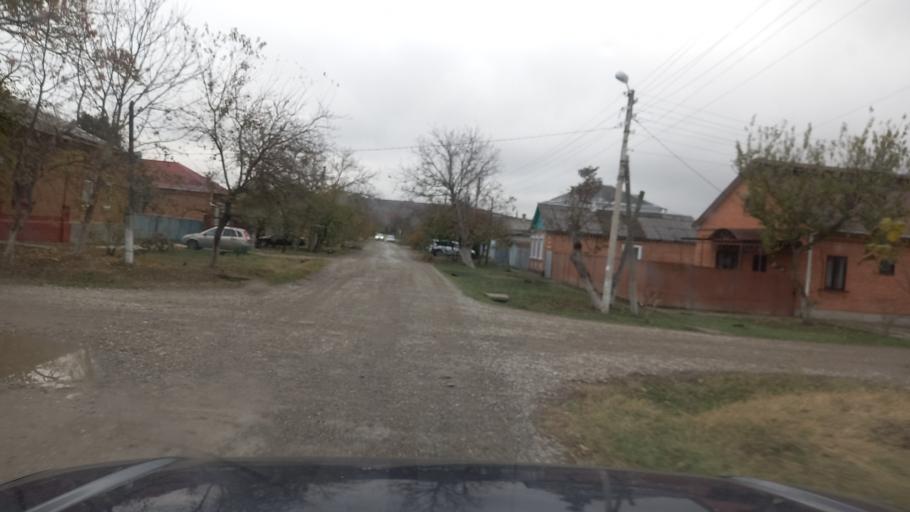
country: RU
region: Adygeya
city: Maykop
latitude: 44.6047
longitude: 40.0849
